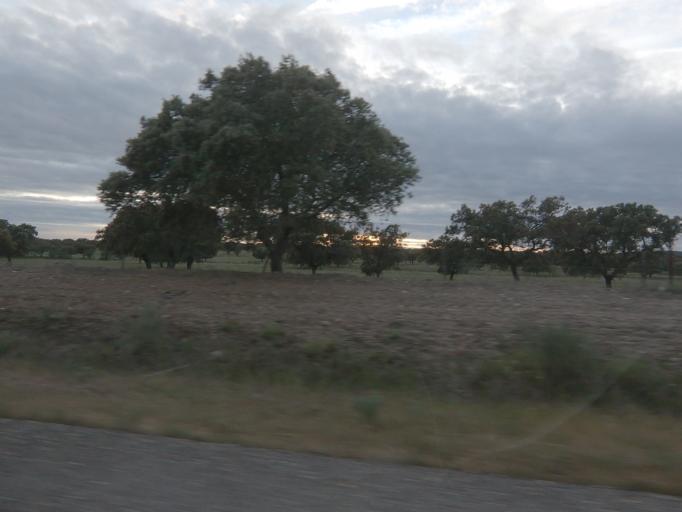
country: ES
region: Extremadura
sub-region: Provincia de Badajoz
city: La Roca de la Sierra
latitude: 39.0981
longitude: -6.7127
